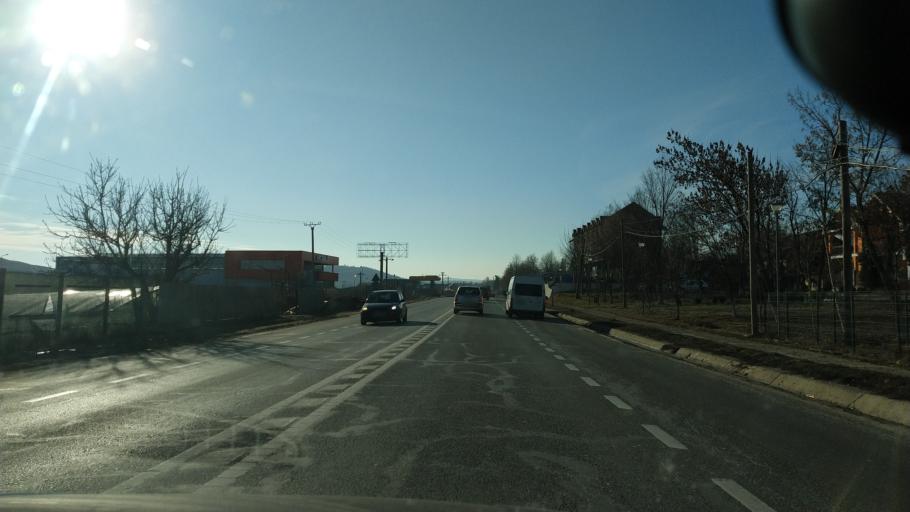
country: RO
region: Iasi
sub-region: Comuna Ion Neculce
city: Razboieni
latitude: 47.2158
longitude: 27.0292
